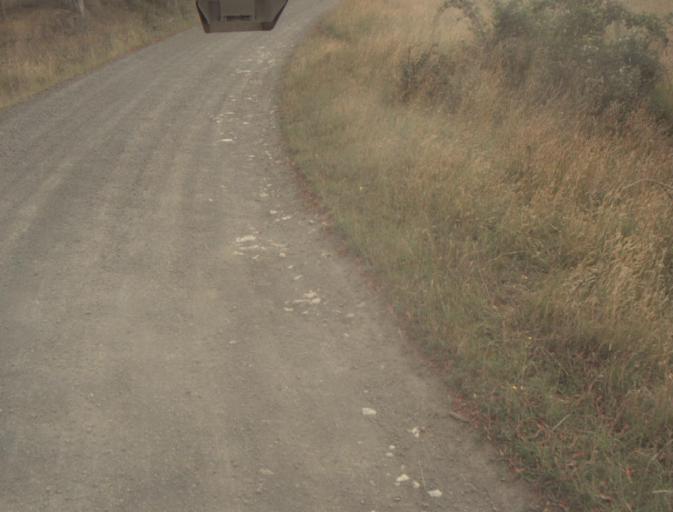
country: AU
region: Tasmania
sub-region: Dorset
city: Scottsdale
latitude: -41.4467
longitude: 147.5863
